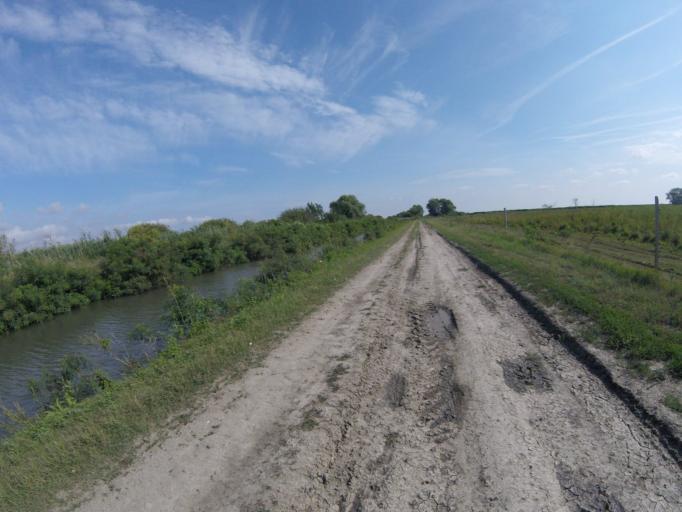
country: HU
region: Hajdu-Bihar
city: Hortobagy
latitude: 47.6184
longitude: 21.0756
